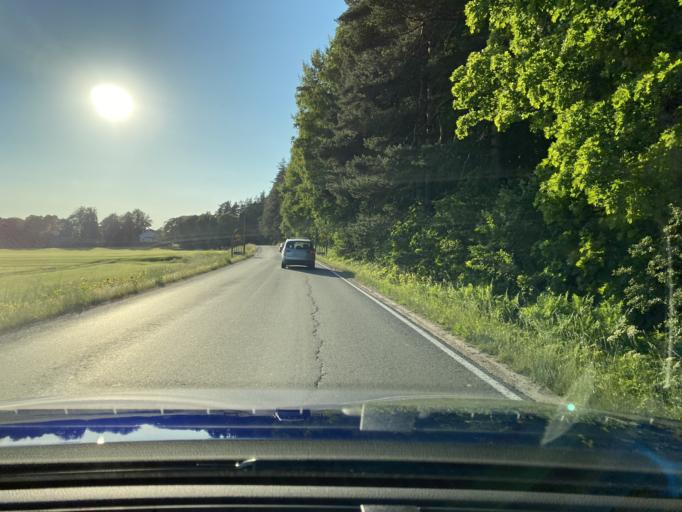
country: FI
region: Haeme
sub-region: Haemeenlinna
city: Tervakoski
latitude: 60.7387
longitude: 24.6611
